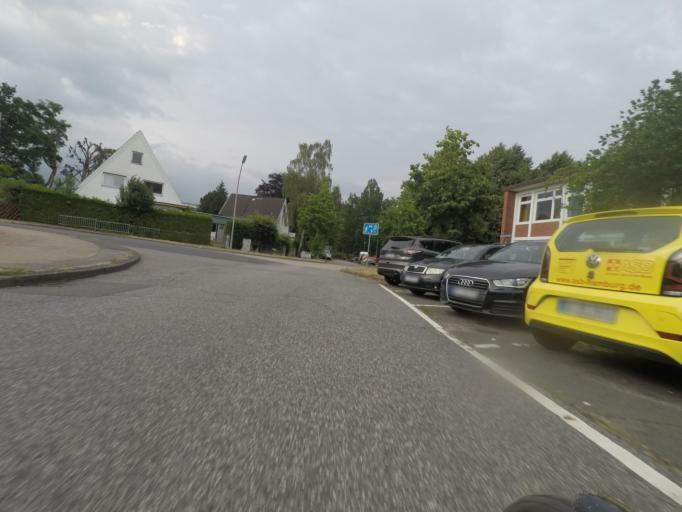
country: DE
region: Hamburg
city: Wandsbek
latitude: 53.5720
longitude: 10.1311
